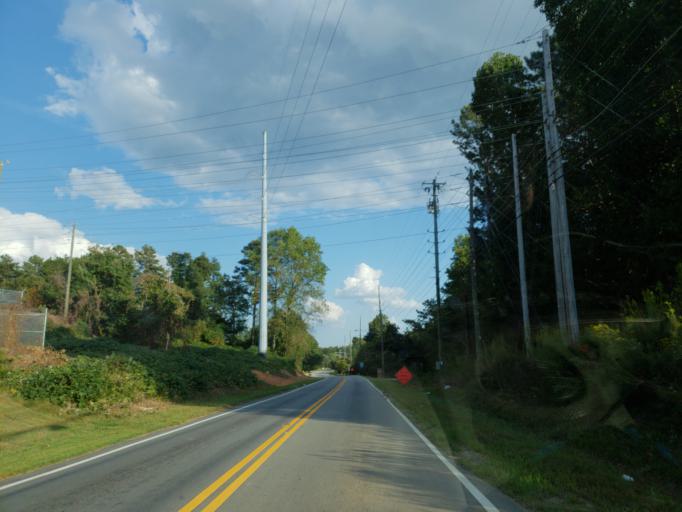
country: US
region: Georgia
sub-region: Cobb County
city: Mableton
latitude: 33.7646
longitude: -84.5952
